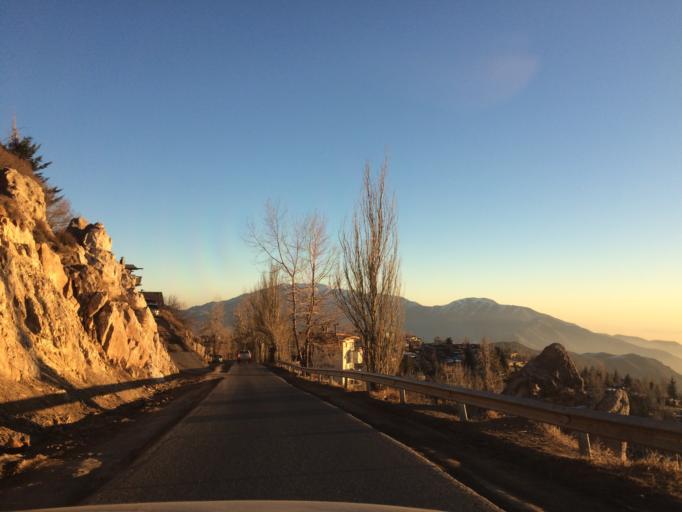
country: CL
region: Santiago Metropolitan
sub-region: Provincia de Santiago
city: Villa Presidente Frei, Nunoa, Santiago, Chile
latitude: -33.3486
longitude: -70.3076
